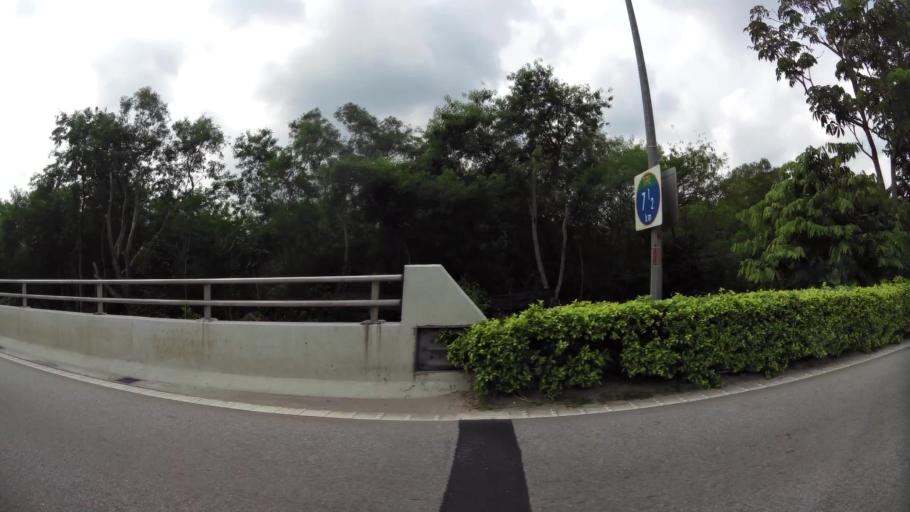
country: MY
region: Johor
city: Kampung Pasir Gudang Baru
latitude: 1.3868
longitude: 103.9133
